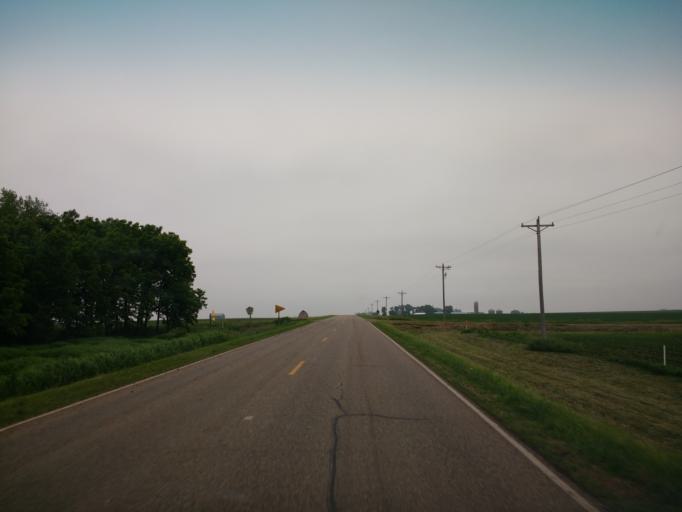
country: US
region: Iowa
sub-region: Sioux County
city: Alton
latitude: 43.0251
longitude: -95.8996
